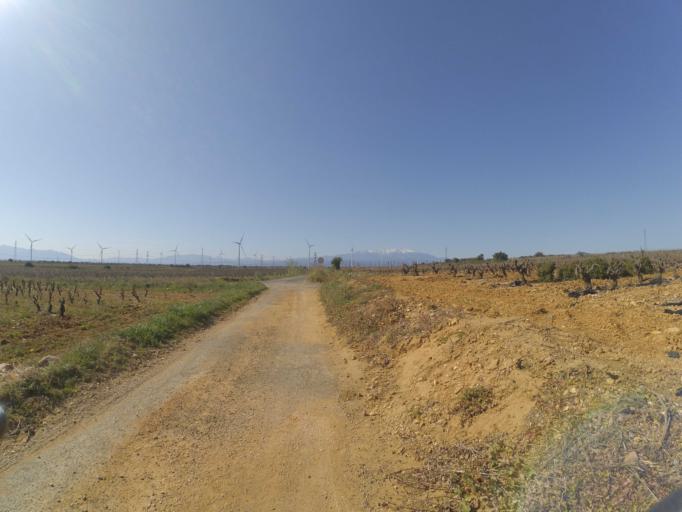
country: FR
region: Languedoc-Roussillon
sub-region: Departement des Pyrenees-Orientales
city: Baixas
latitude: 42.7381
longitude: 2.7927
